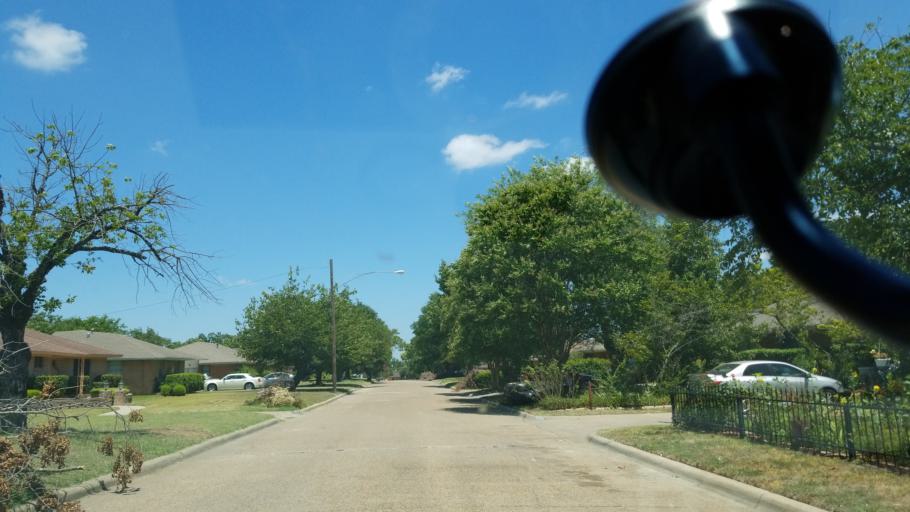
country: US
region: Texas
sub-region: Dallas County
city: Cockrell Hill
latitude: 32.6767
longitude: -96.8182
